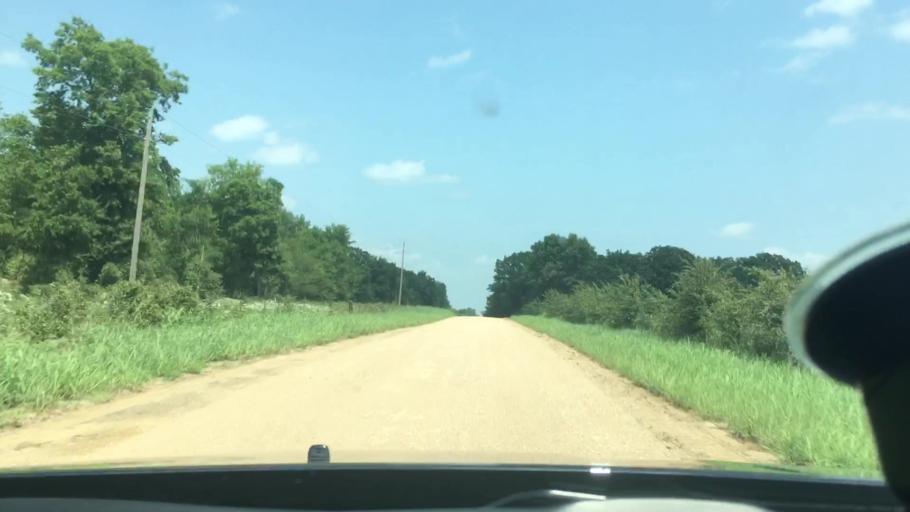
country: US
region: Oklahoma
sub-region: Coal County
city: Coalgate
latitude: 34.4250
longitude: -96.4677
